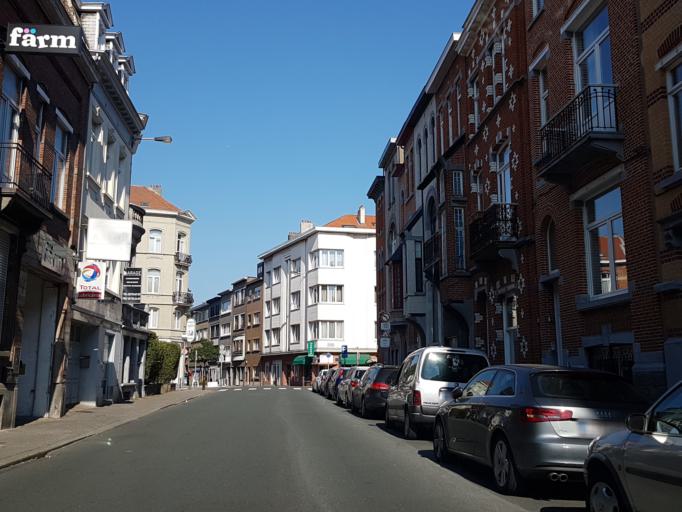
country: BE
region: Brussels Capital
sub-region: Bruxelles-Capitale
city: Brussels
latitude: 50.8422
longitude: 4.4012
